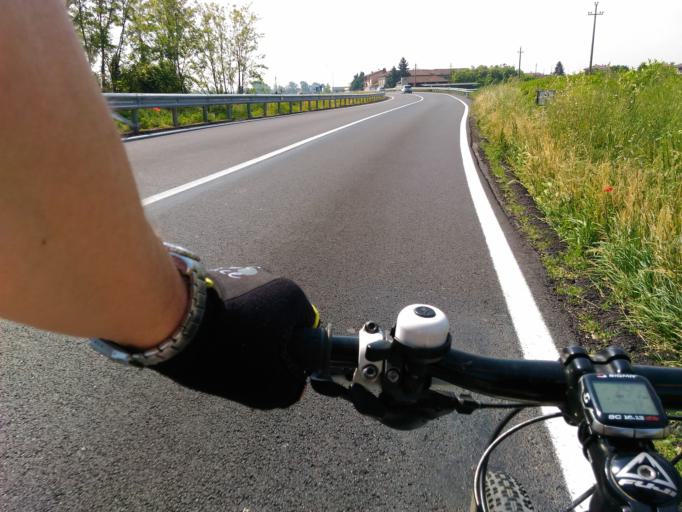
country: IT
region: Lombardy
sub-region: Provincia di Lodi
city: Marudo
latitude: 45.2739
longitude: 9.3830
